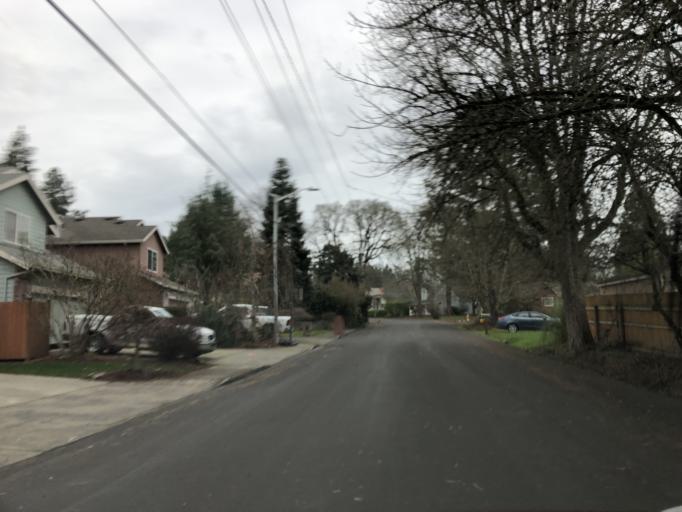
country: US
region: Oregon
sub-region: Washington County
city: Tigard
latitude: 45.4328
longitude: -122.7751
